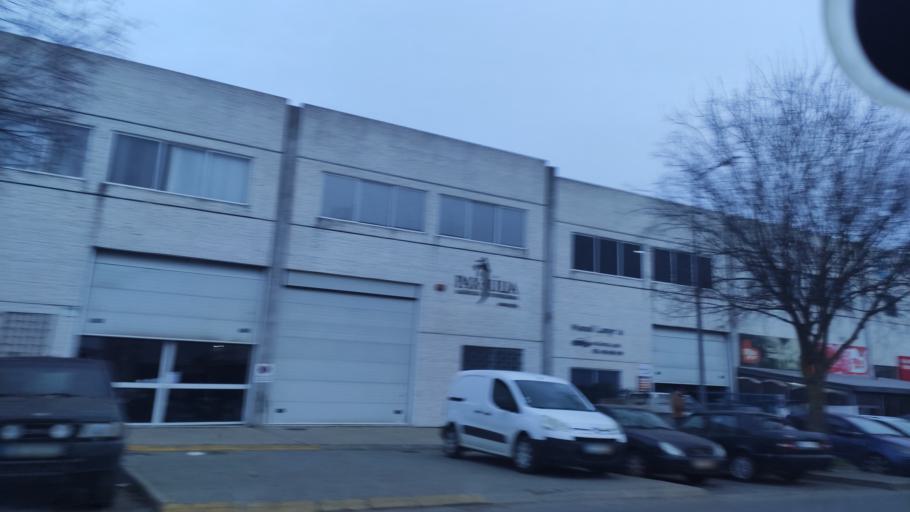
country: PT
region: Beja
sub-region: Beja
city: Beja
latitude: 38.0199
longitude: -7.8525
